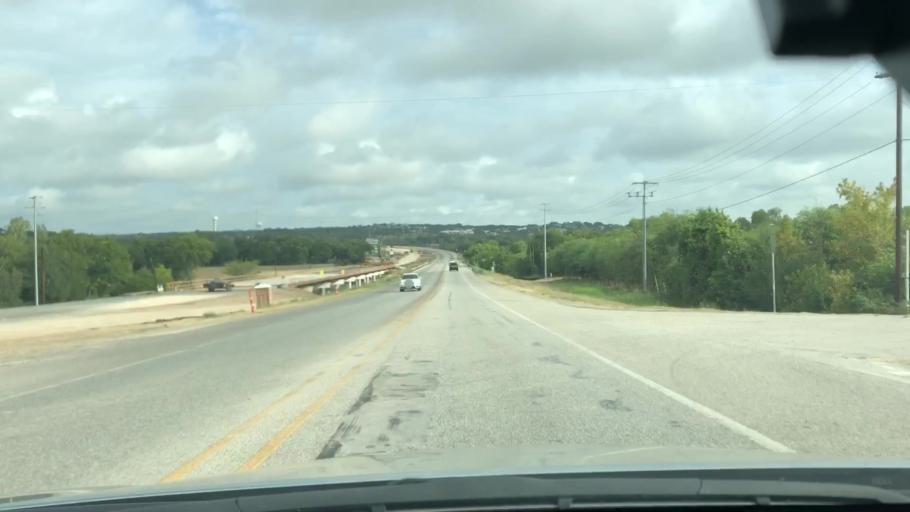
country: US
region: Texas
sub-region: Comal County
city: New Braunfels
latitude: 29.6857
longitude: -98.1543
